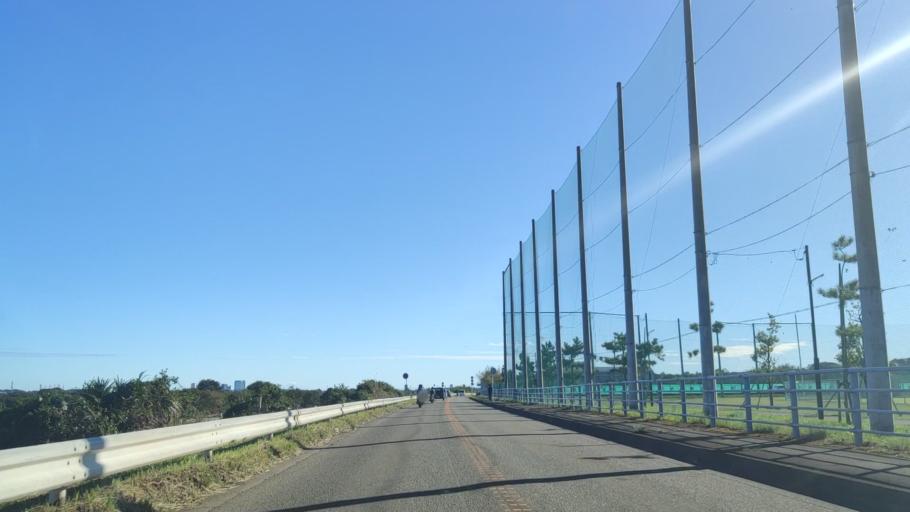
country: JP
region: Kanagawa
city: Zama
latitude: 35.5102
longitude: 139.3742
